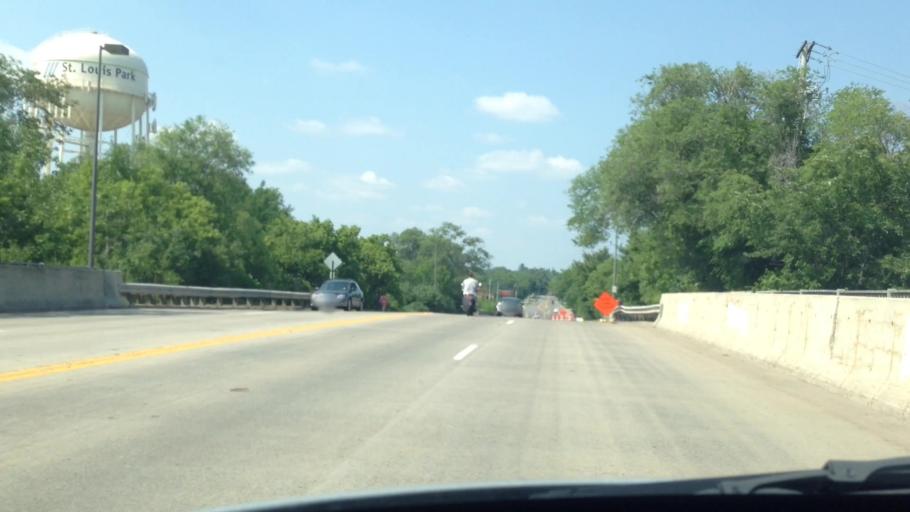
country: US
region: Minnesota
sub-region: Hennepin County
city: Saint Louis Park
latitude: 44.9568
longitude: -93.3709
